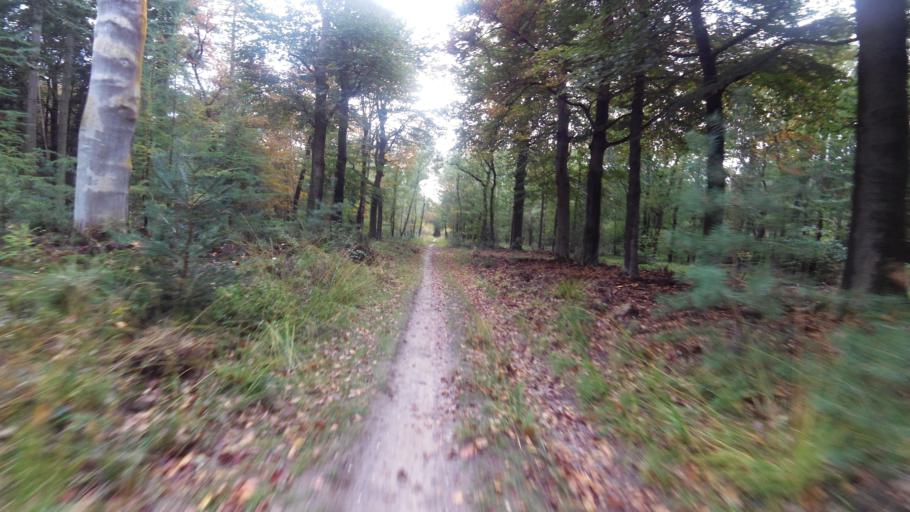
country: NL
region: Gelderland
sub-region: Gemeente Ede
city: Wekerom
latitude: 52.0707
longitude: 5.7122
